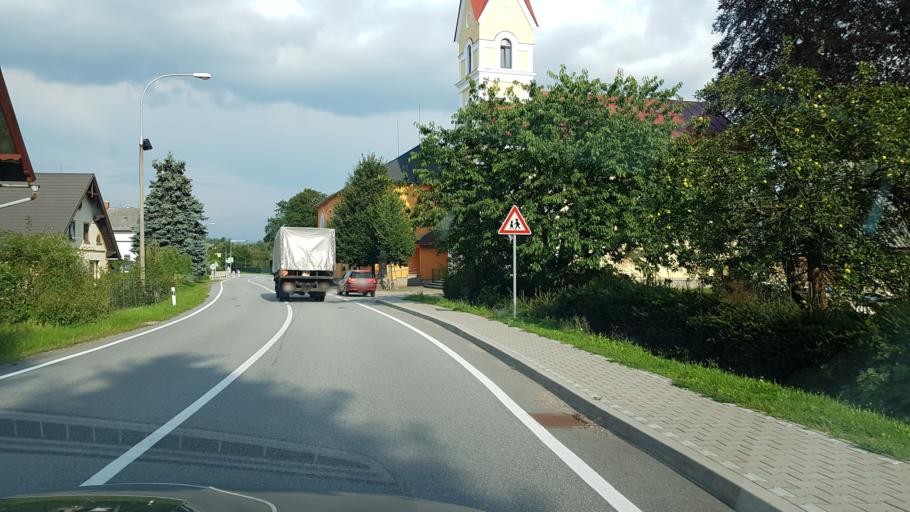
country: PL
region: Lower Silesian Voivodeship
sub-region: Powiat klodzki
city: Miedzylesie
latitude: 50.0977
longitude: 16.6650
